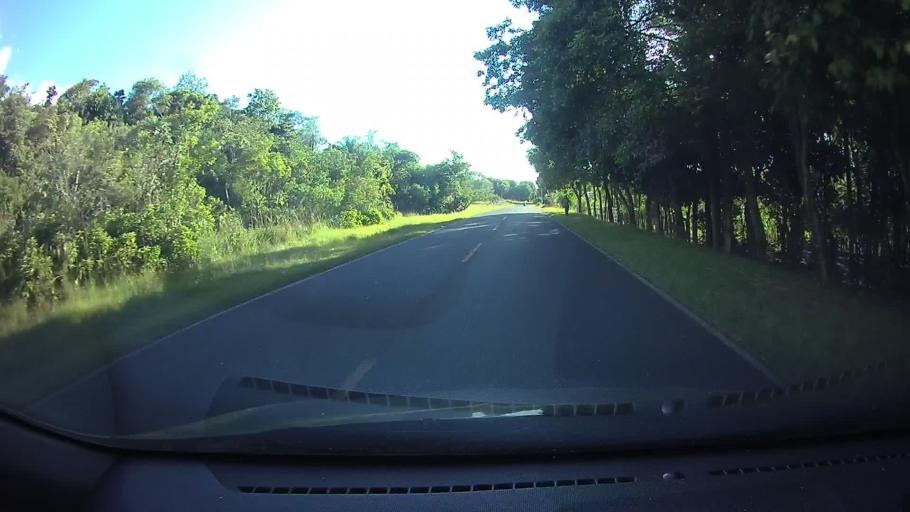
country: PY
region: Cordillera
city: Emboscada
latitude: -25.1720
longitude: -57.2808
